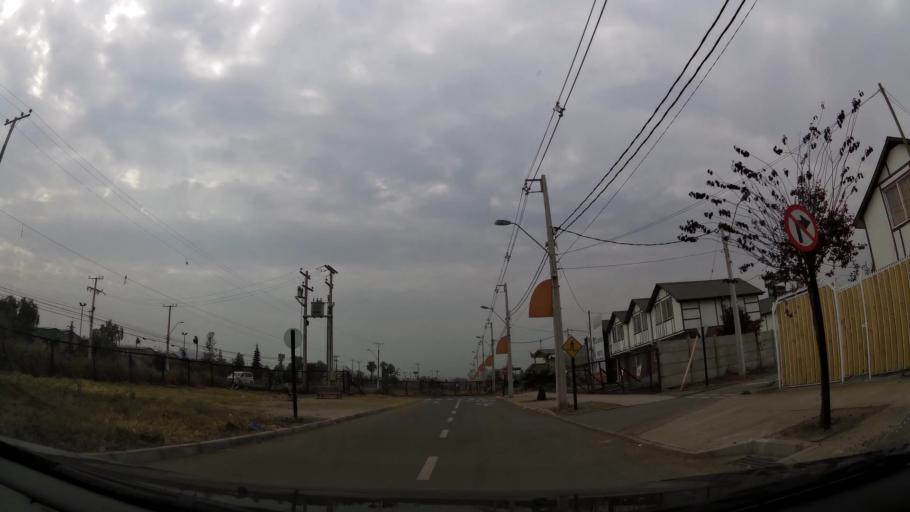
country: CL
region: Santiago Metropolitan
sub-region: Provincia de Chacabuco
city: Chicureo Abajo
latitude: -33.1966
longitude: -70.6690
